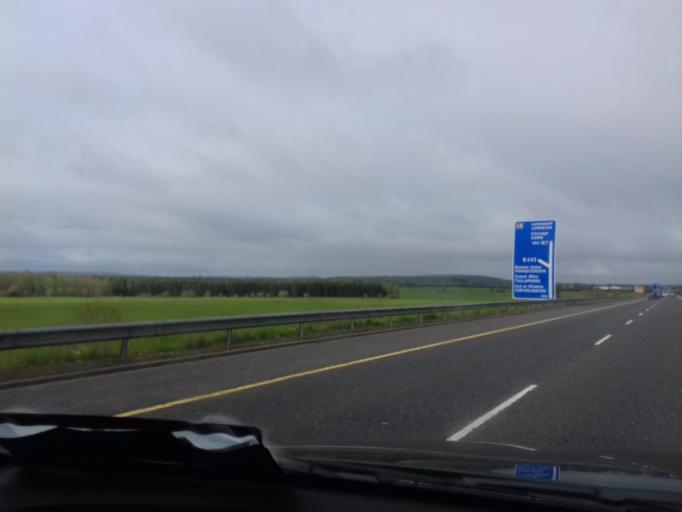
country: IE
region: Leinster
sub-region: Kildare
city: Cherryville
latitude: 53.1495
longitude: -6.9896
